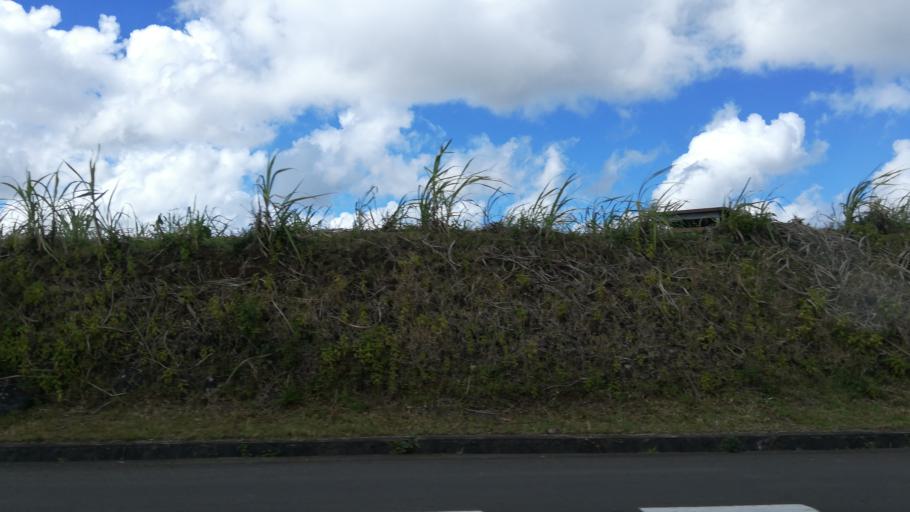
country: MU
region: Moka
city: Providence
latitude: -20.2435
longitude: 57.6154
